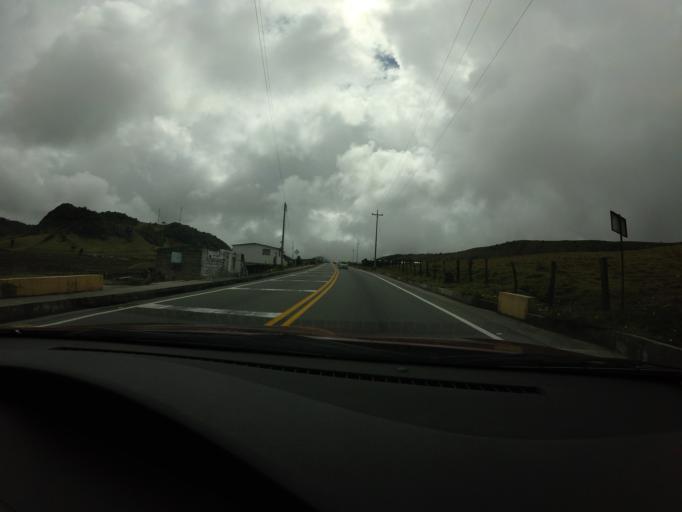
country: CO
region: Tolima
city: Herveo
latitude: 5.0498
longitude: -75.3286
